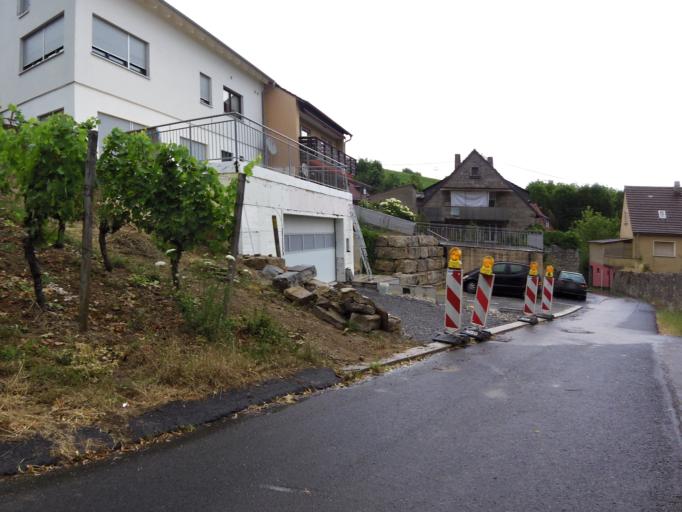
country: DE
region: Bavaria
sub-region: Regierungsbezirk Unterfranken
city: Randersacker
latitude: 49.7622
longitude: 9.9799
